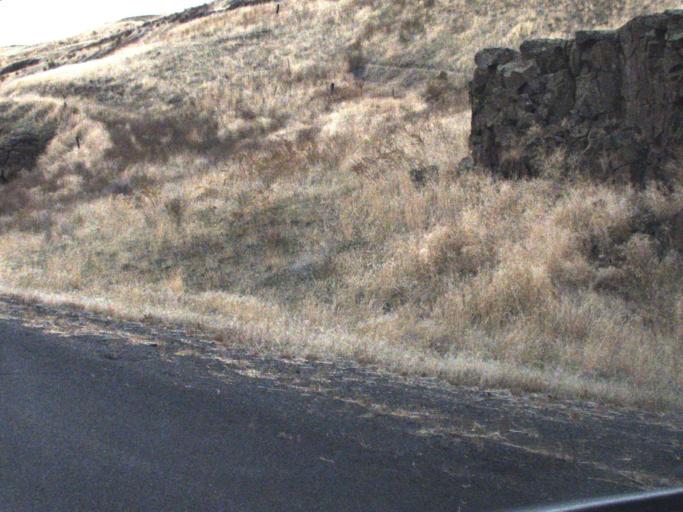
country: US
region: Washington
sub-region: Adams County
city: Ritzville
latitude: 46.7504
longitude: -118.1952
